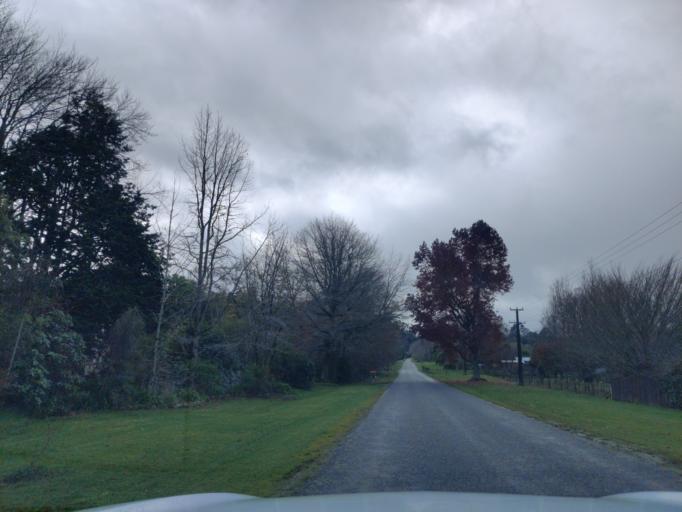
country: NZ
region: Manawatu-Wanganui
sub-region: Palmerston North City
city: Palmerston North
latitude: -40.1728
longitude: 175.7958
